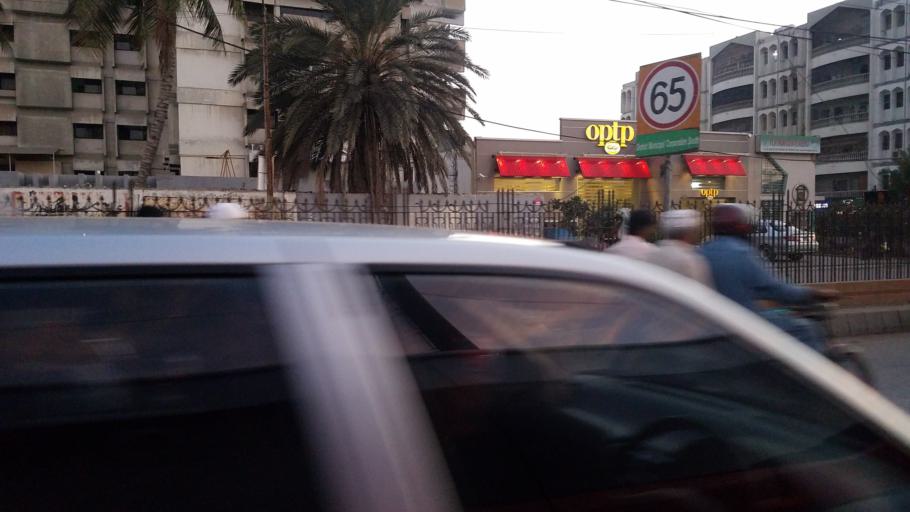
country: PK
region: Sindh
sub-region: Karachi District
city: Karachi
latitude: 24.8274
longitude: 67.0314
